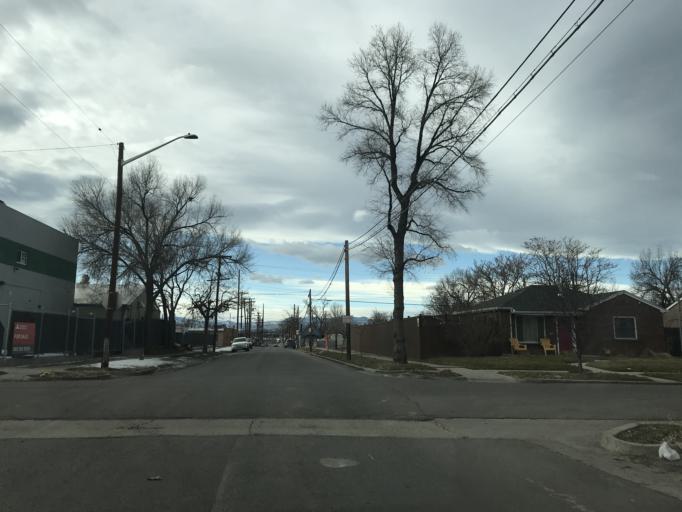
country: US
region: Colorado
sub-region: Adams County
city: Commerce City
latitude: 39.7764
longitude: -104.9552
